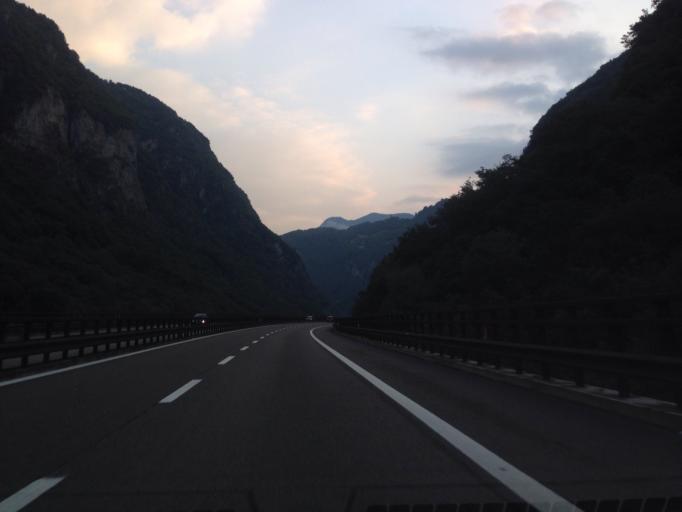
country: IT
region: Trentino-Alto Adige
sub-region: Bolzano
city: Fie Allo Sciliar
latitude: 46.5413
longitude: 11.5043
